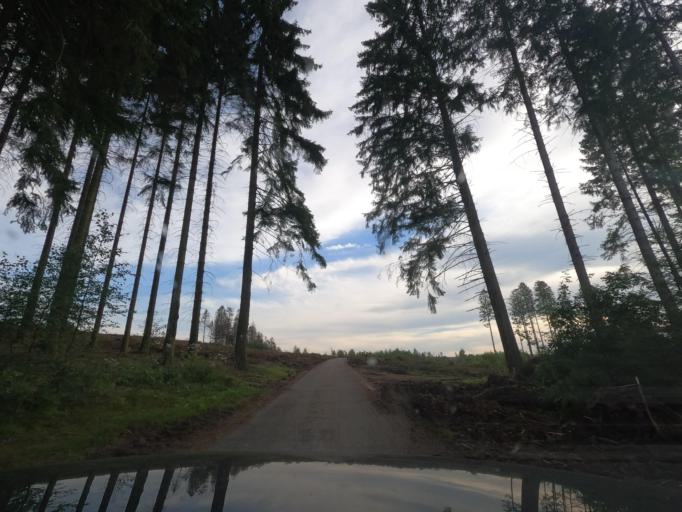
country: DE
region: North Rhine-Westphalia
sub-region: Regierungsbezirk Arnsberg
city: Herscheid
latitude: 51.1986
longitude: 7.7495
